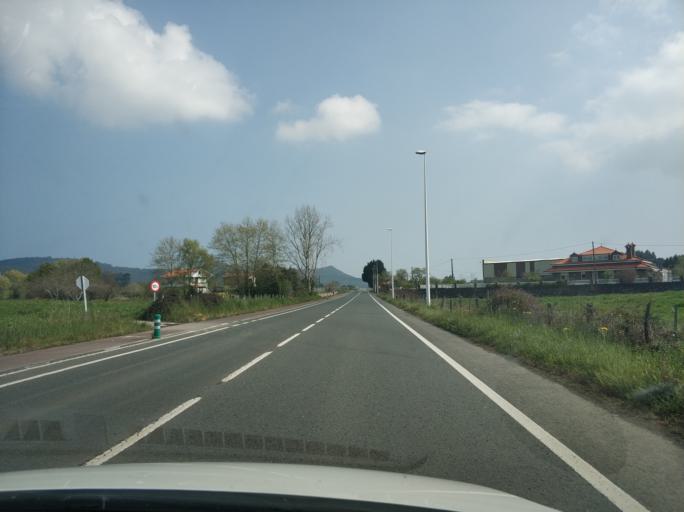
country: ES
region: Cantabria
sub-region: Provincia de Cantabria
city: Escalante
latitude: 43.4394
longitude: -3.5079
